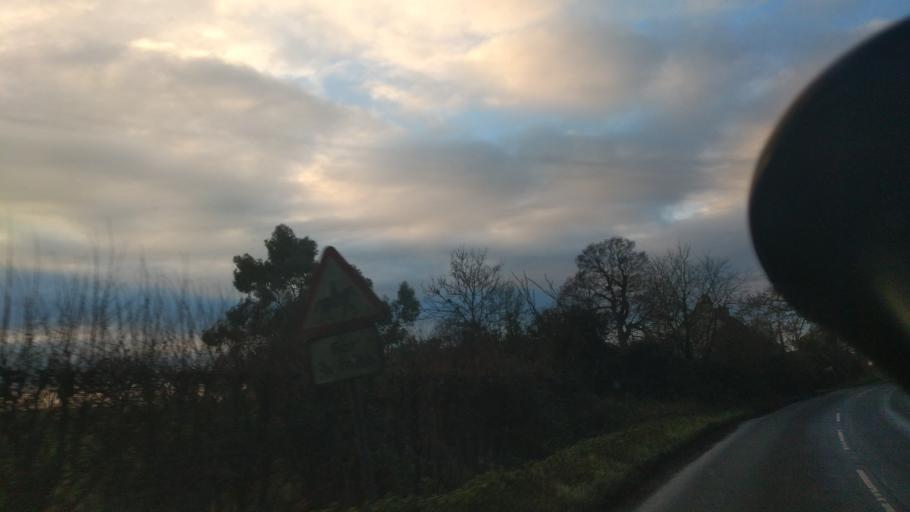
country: GB
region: England
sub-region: Wiltshire
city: Wingfield
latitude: 51.3028
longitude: -2.2583
